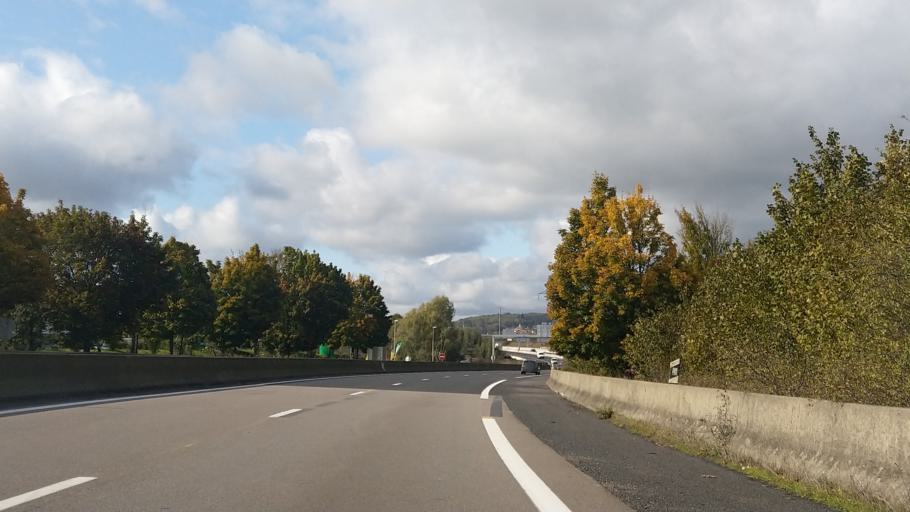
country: FR
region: Ile-de-France
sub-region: Departement du Val-d'Oise
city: Attainville
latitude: 49.0599
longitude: 2.3497
